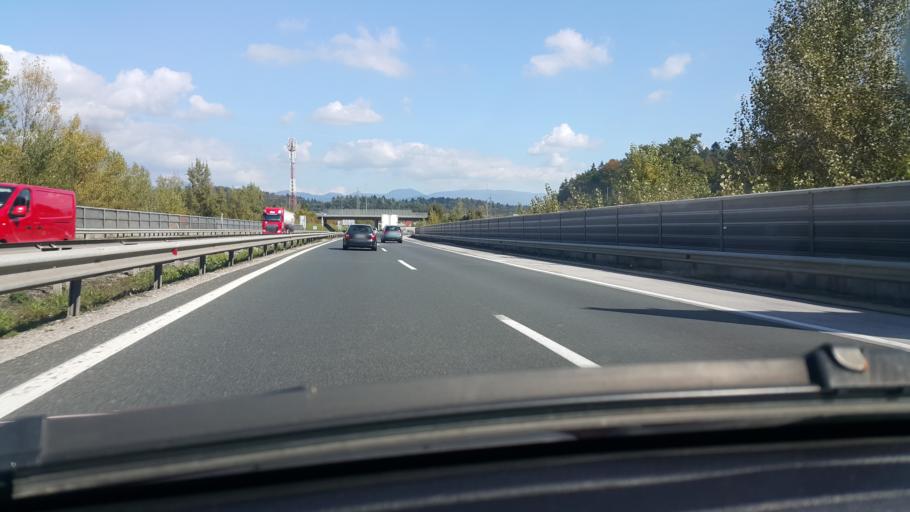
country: SI
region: Domzale
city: Domzale
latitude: 46.1296
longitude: 14.6076
